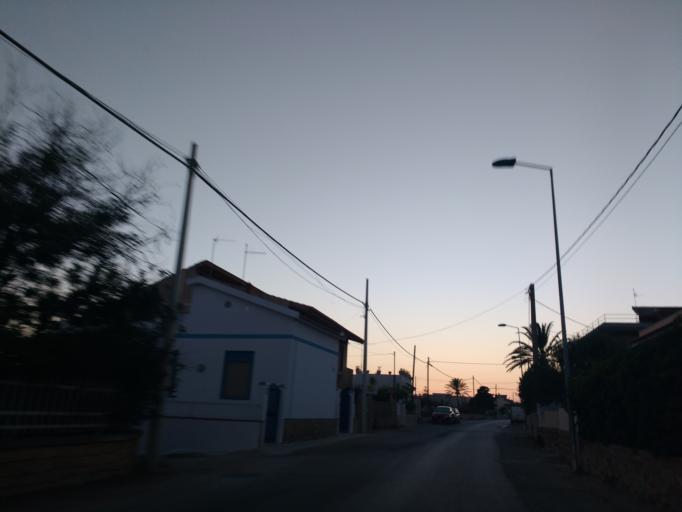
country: IT
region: Sicily
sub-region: Ragusa
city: Cava d'Aliga
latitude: 36.7238
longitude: 14.6941
